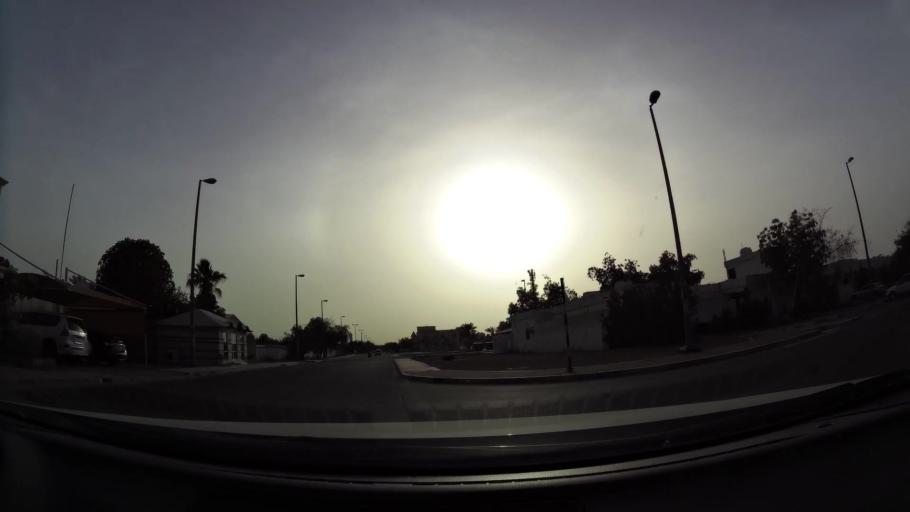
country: OM
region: Al Buraimi
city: Al Buraymi
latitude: 24.2453
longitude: 55.7471
